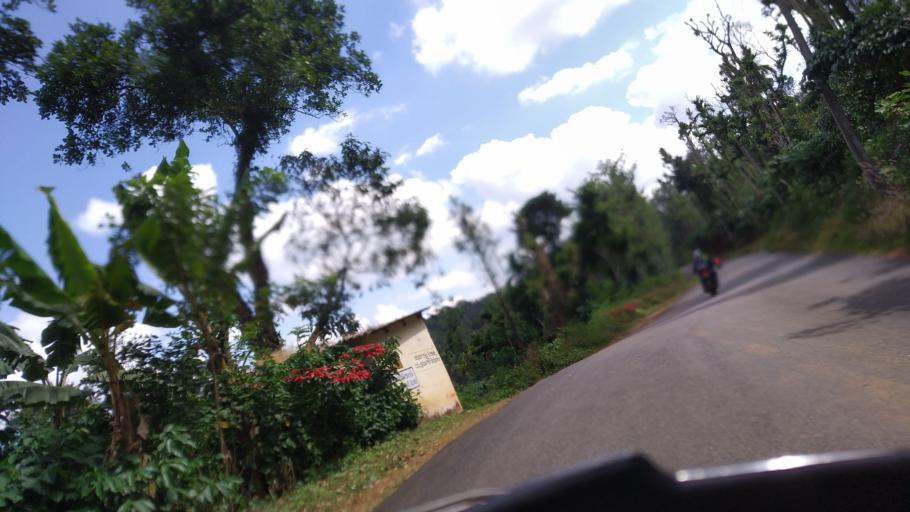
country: IN
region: Karnataka
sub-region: Kodagu
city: Ponnampet
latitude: 12.0361
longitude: 75.9179
